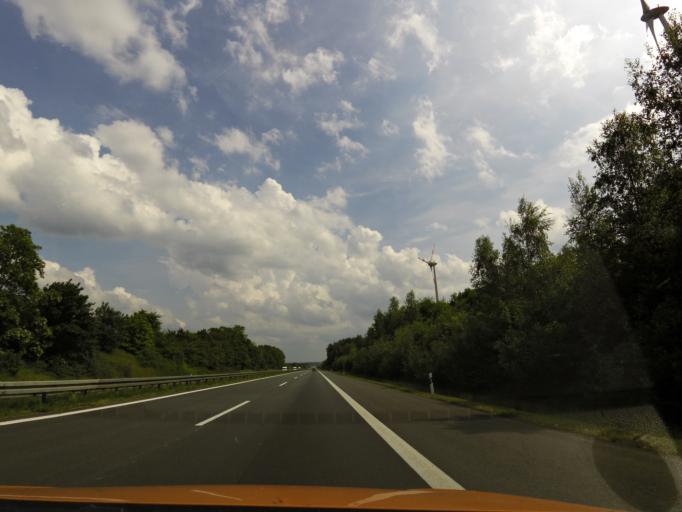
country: DE
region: Brandenburg
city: Gerdshagen
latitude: 53.2206
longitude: 12.2325
